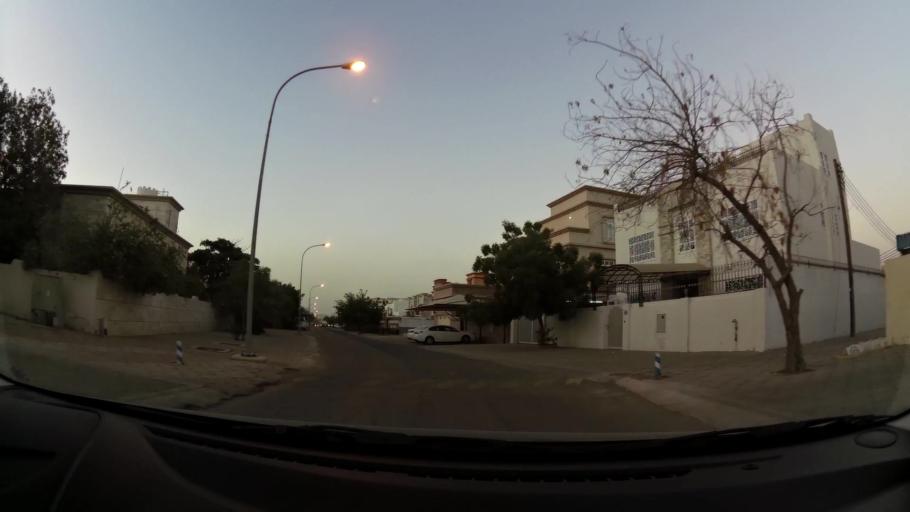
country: OM
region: Muhafazat Masqat
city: As Sib al Jadidah
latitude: 23.5995
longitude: 58.2356
